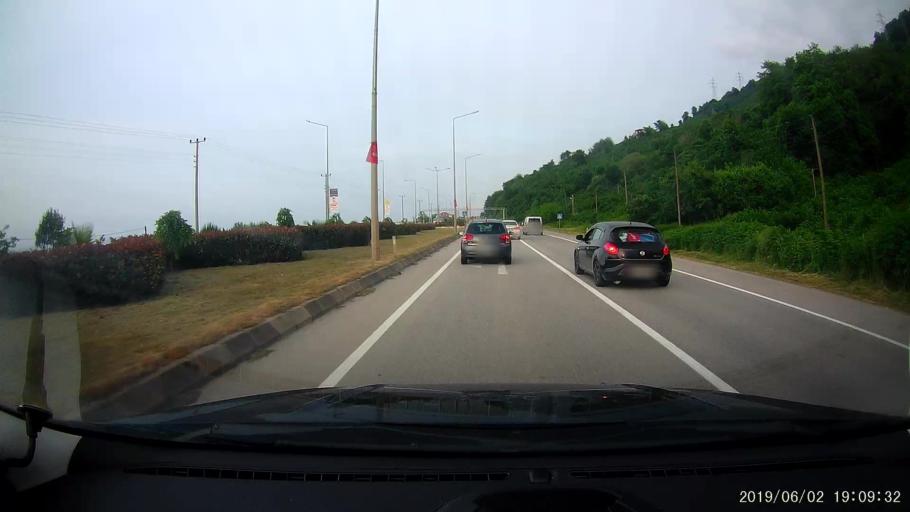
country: TR
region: Ordu
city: Gulyali
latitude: 40.9726
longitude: 38.0301
